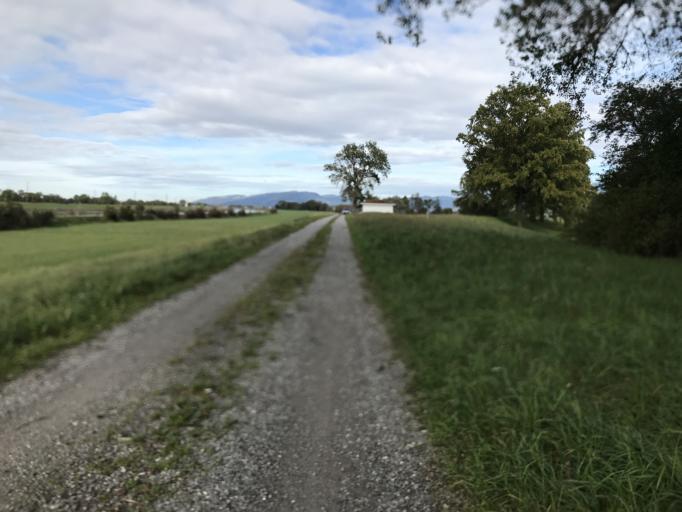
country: AT
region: Vorarlberg
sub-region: Politischer Bezirk Feldkirch
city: Mader
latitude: 47.3672
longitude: 9.6280
